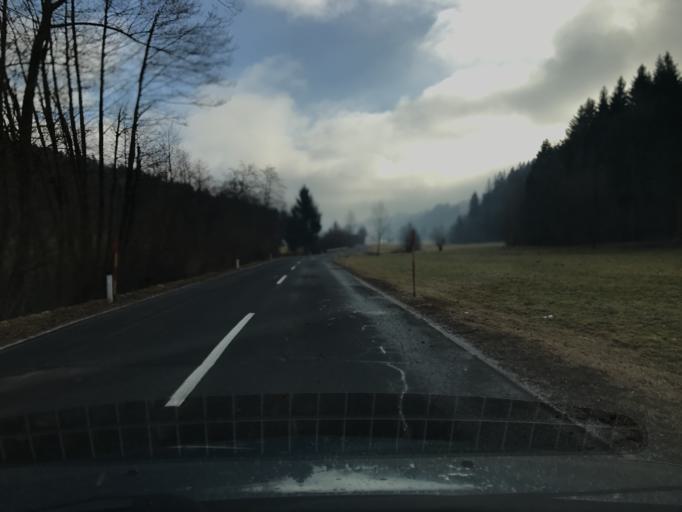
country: SI
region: Lukovica
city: Lukovica pri Domzalah
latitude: 46.2186
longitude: 14.7432
